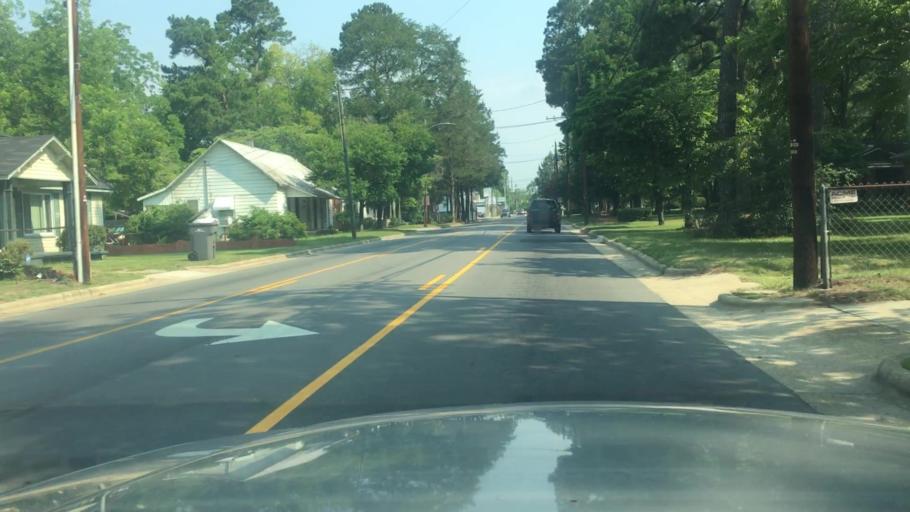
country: US
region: North Carolina
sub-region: Cumberland County
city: Hope Mills
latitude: 34.9685
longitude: -78.9448
